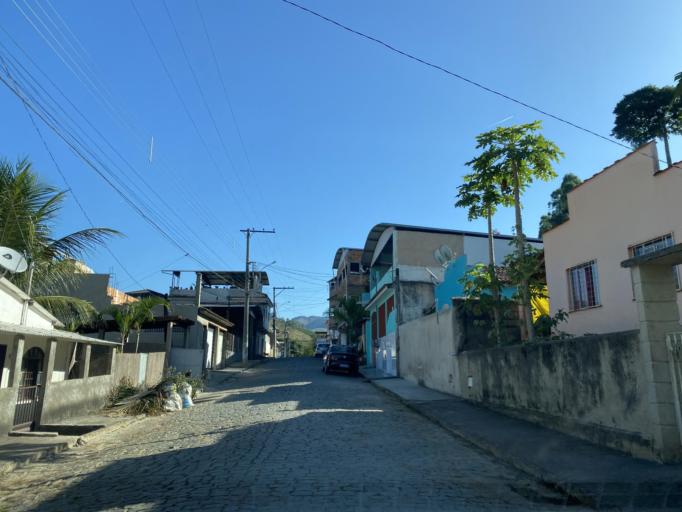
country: BR
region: Espirito Santo
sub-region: Jeronimo Monteiro
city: Jeronimo Monteiro
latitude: -20.7916
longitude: -41.4005
